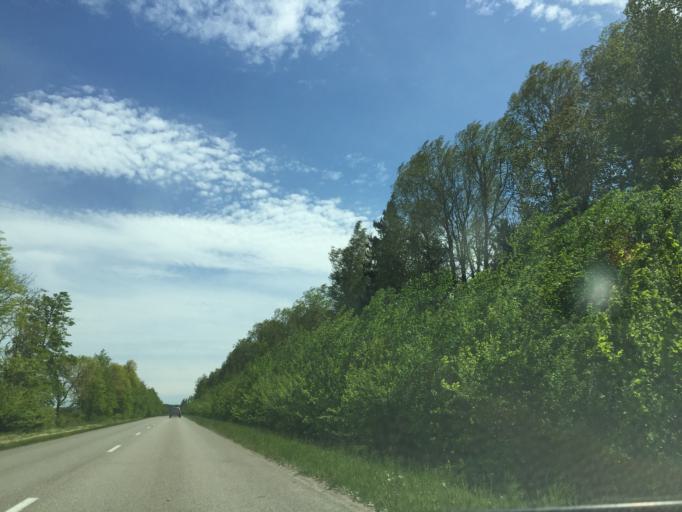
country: LT
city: Linkuva
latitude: 56.0395
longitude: 24.1395
